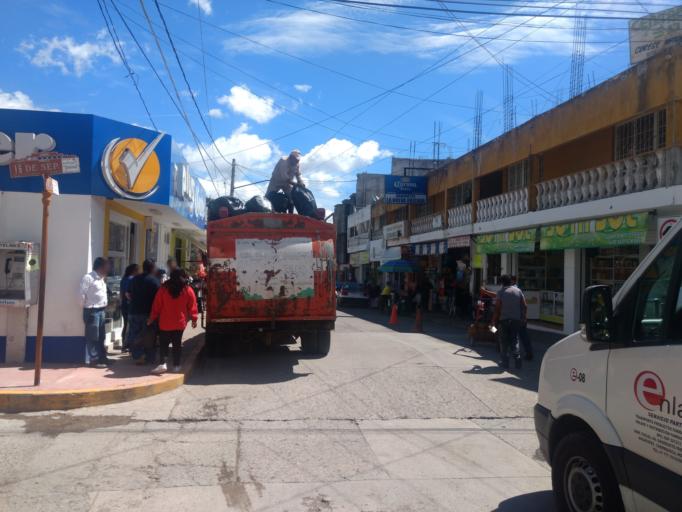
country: MX
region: Oaxaca
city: Ciudad de Huajuapam de Leon
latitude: 17.8088
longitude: -97.7766
